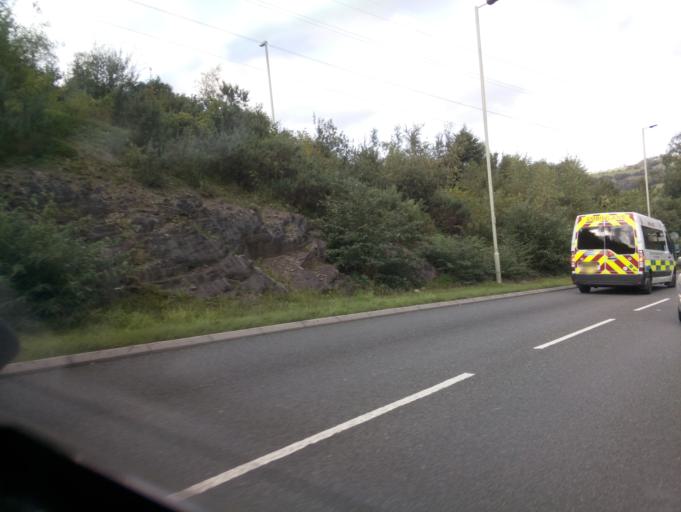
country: GB
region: Wales
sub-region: Rhondda Cynon Taf
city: Llantwit Fardre
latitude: 51.5741
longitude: -3.3038
